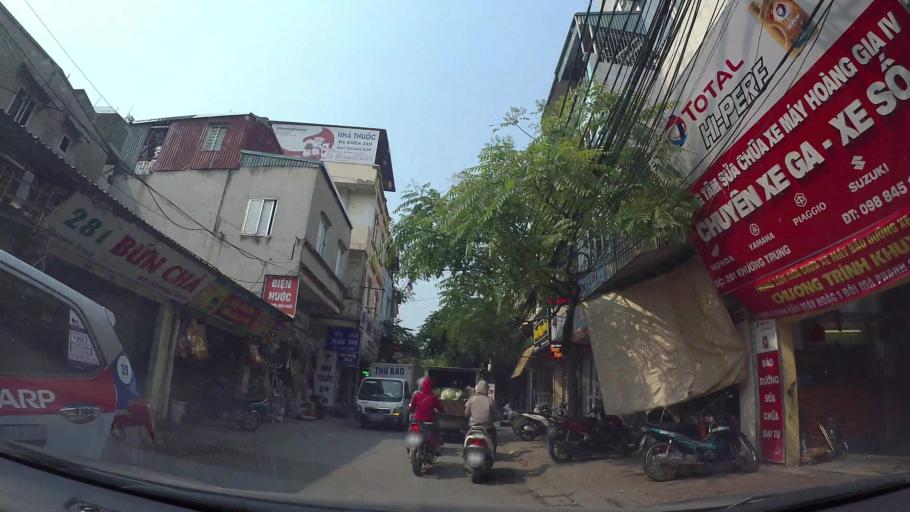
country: VN
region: Ha Noi
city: Thanh Xuan
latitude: 20.9945
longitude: 105.8174
